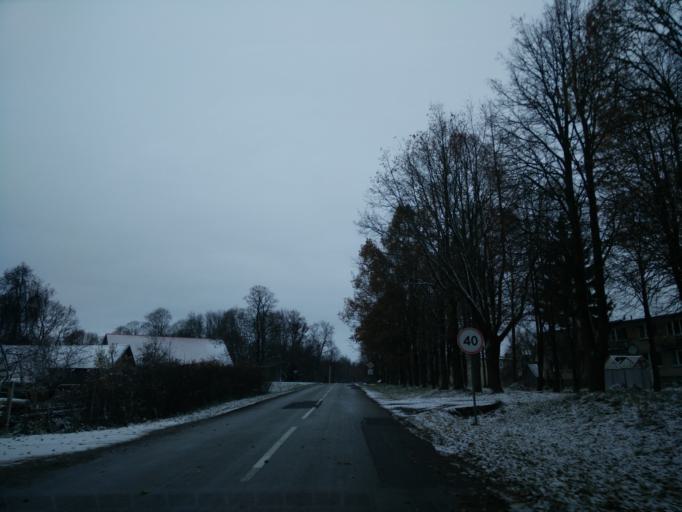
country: LT
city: Tytuveneliai
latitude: 55.4884
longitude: 23.3303
